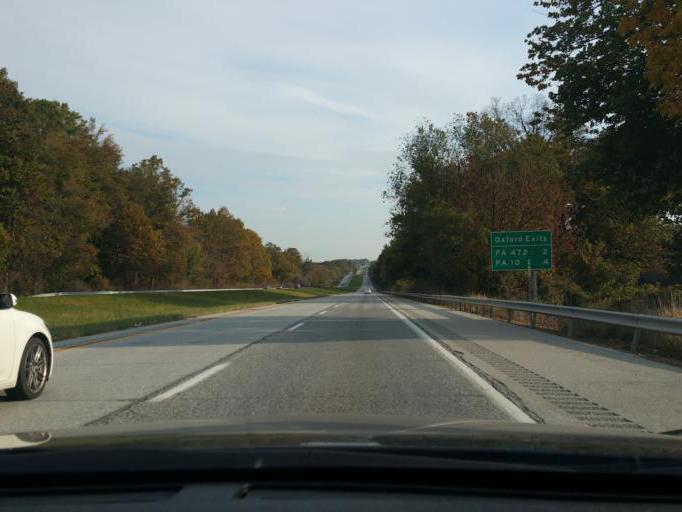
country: US
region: Pennsylvania
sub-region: Chester County
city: Oxford
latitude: 39.7623
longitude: -76.0177
